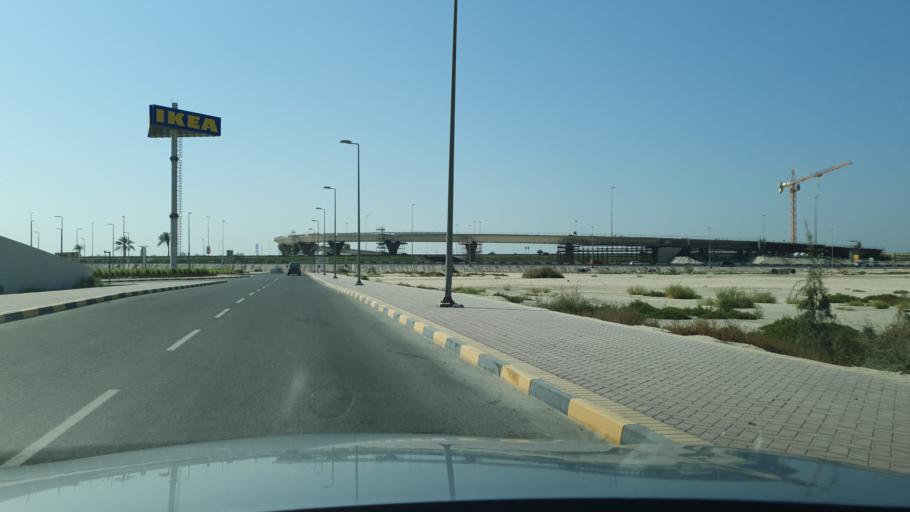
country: BH
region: Northern
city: Madinat `Isa
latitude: 26.1807
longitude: 50.5055
